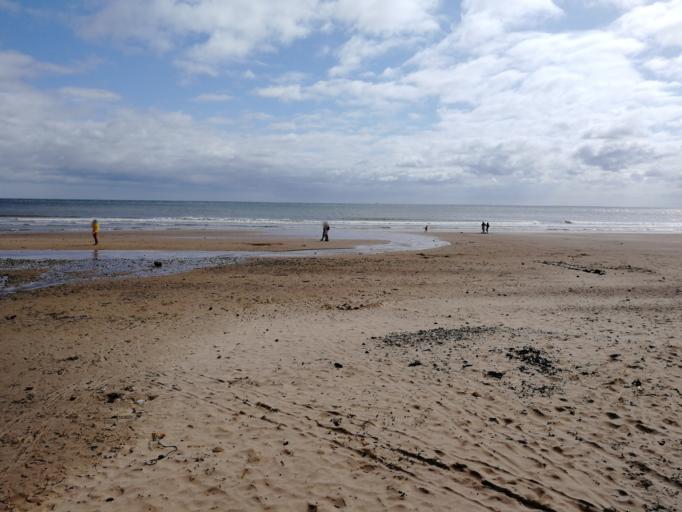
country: GB
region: England
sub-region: North Yorkshire
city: Filey
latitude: 54.1951
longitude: -0.2832
